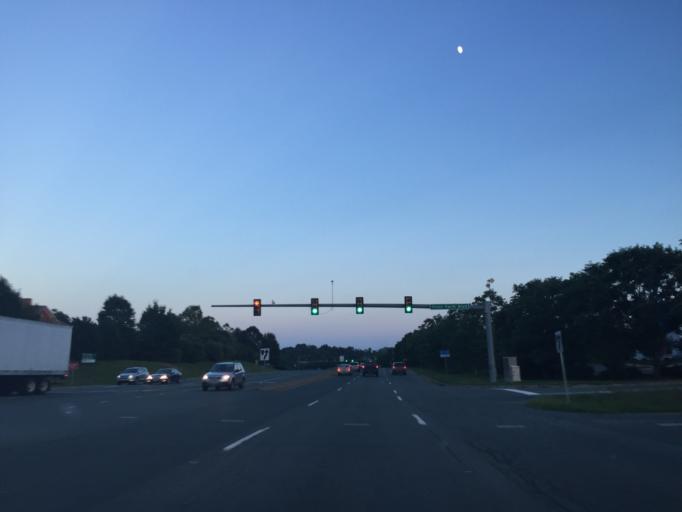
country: US
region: Virginia
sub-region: City of Charlottesville
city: Charlottesville
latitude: 38.0288
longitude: -78.4411
